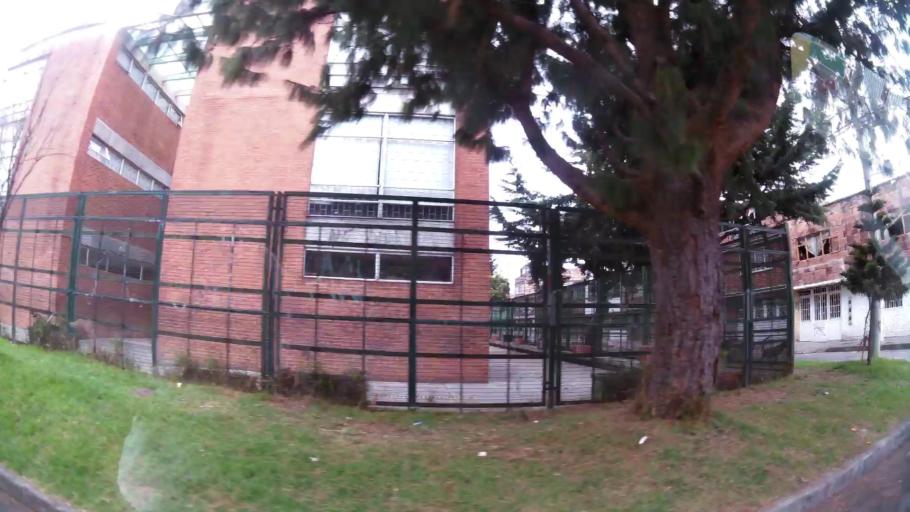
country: CO
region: Bogota D.C.
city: Barrio San Luis
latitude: 4.7030
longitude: -74.0965
